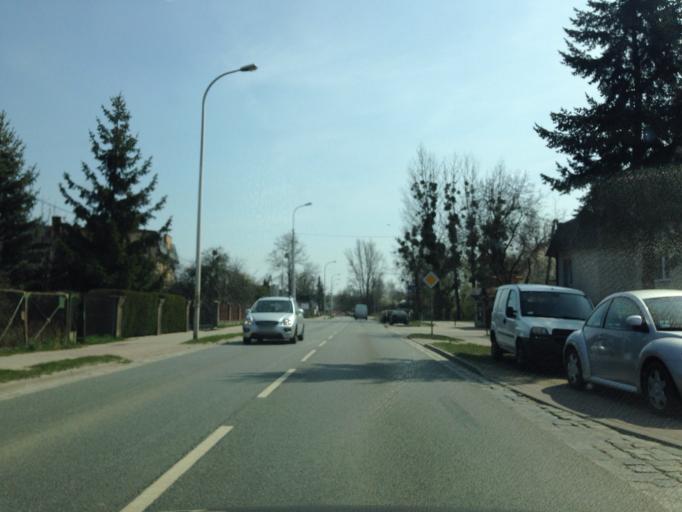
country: PL
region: Lower Silesian Voivodeship
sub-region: Powiat wroclawski
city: Wilczyce
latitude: 51.1072
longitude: 17.1423
